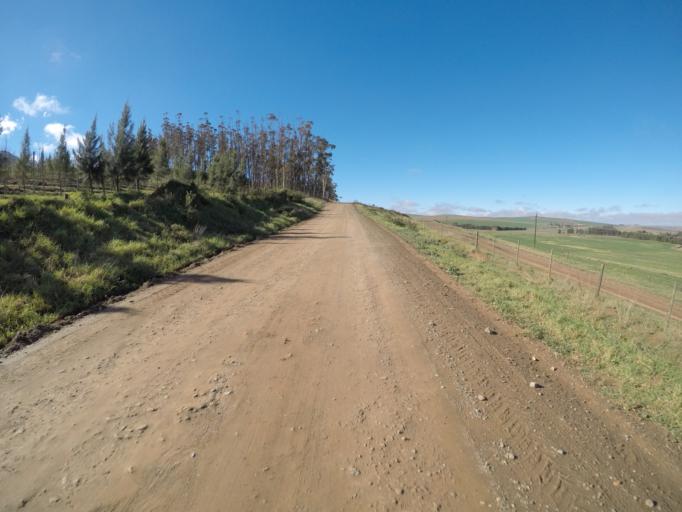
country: ZA
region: Western Cape
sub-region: Overberg District Municipality
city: Caledon
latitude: -34.0956
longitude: 19.6894
